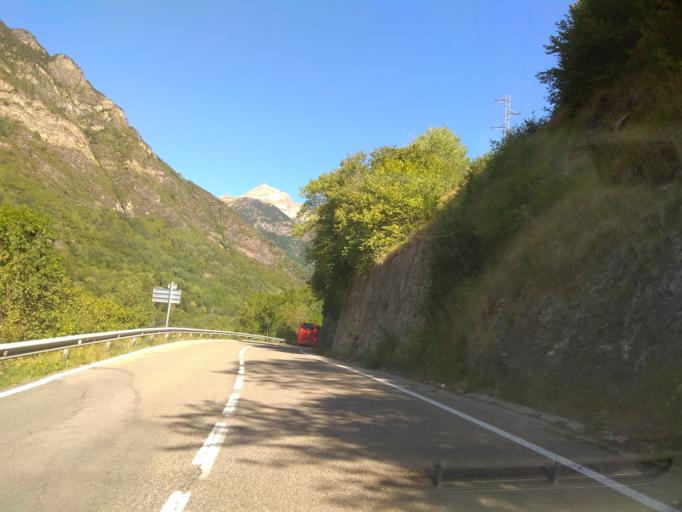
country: ES
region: Catalonia
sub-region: Provincia de Lleida
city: Vielha
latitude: 42.5281
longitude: 0.8337
